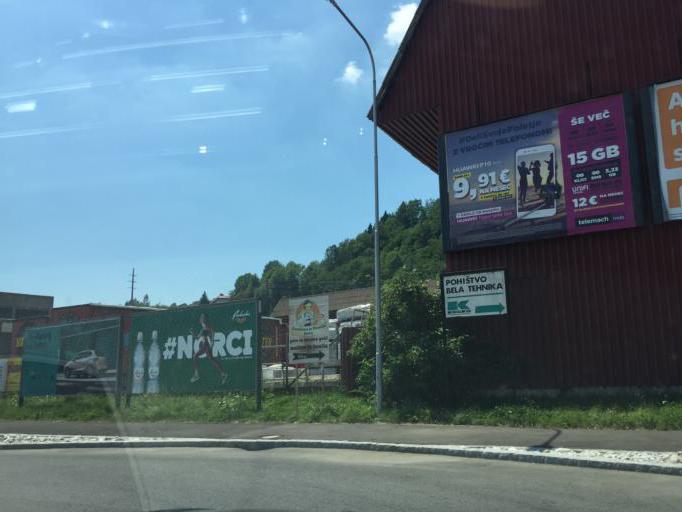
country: SI
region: Kranj
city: Kranj
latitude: 46.2416
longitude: 14.3490
